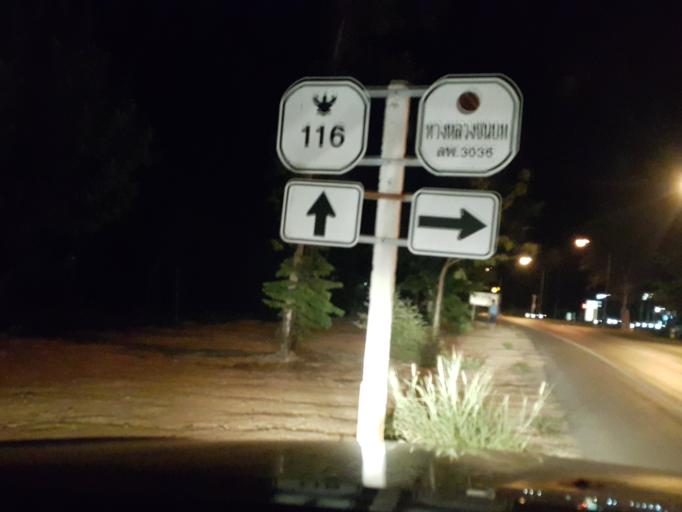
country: TH
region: Lamphun
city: Pa Sang
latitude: 18.4692
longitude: 98.9678
